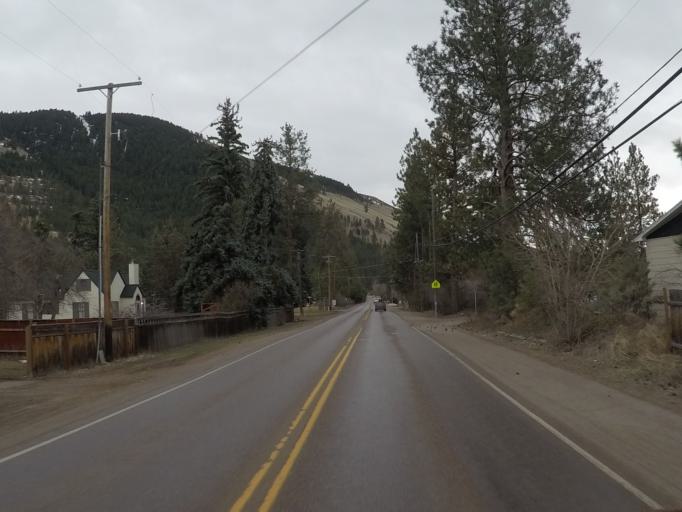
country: US
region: Montana
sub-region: Missoula County
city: East Missoula
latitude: 46.8901
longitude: -113.9657
